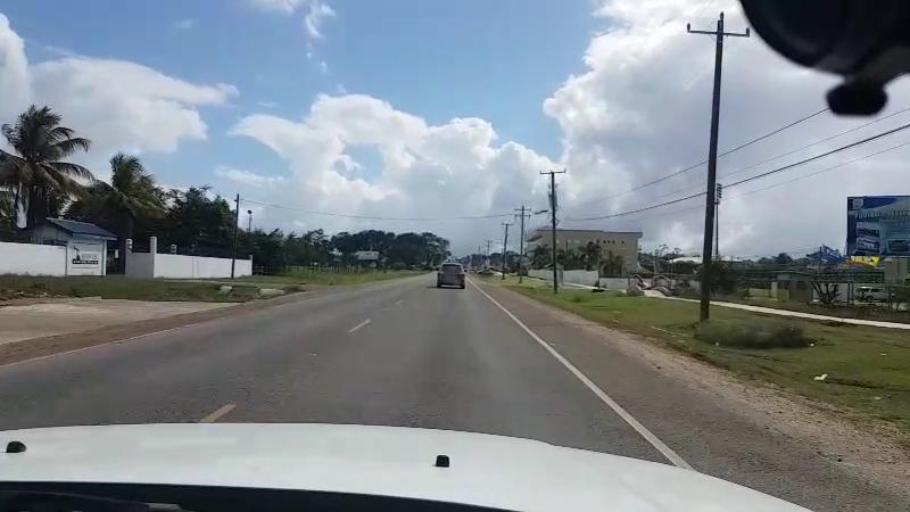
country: BZ
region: Cayo
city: Belmopan
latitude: 17.2538
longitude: -88.7856
